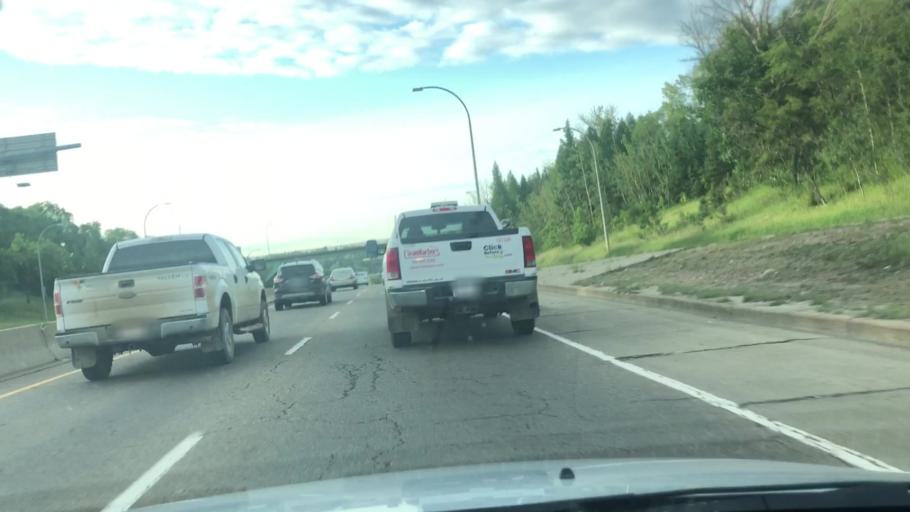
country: CA
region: Alberta
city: Edmonton
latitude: 53.5617
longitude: -113.4451
